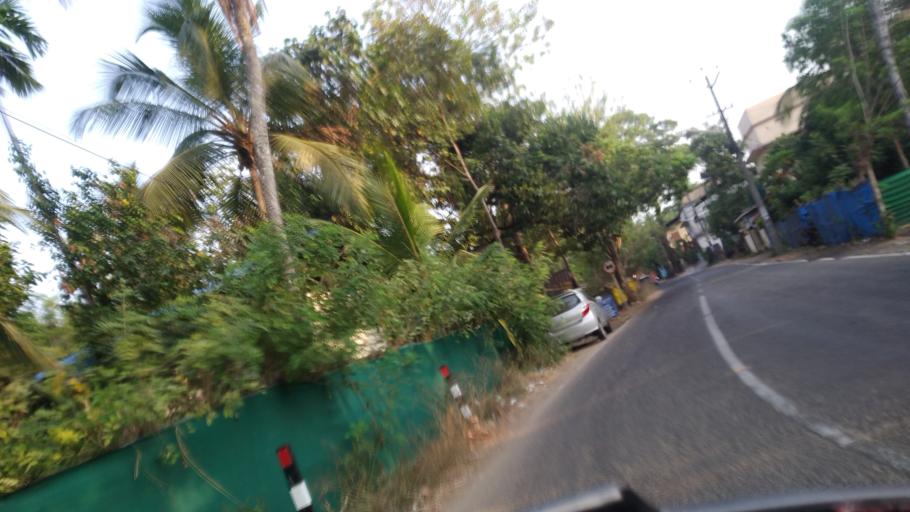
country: IN
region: Kerala
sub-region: Thrissur District
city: Thanniyam
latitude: 10.4104
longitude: 76.0941
